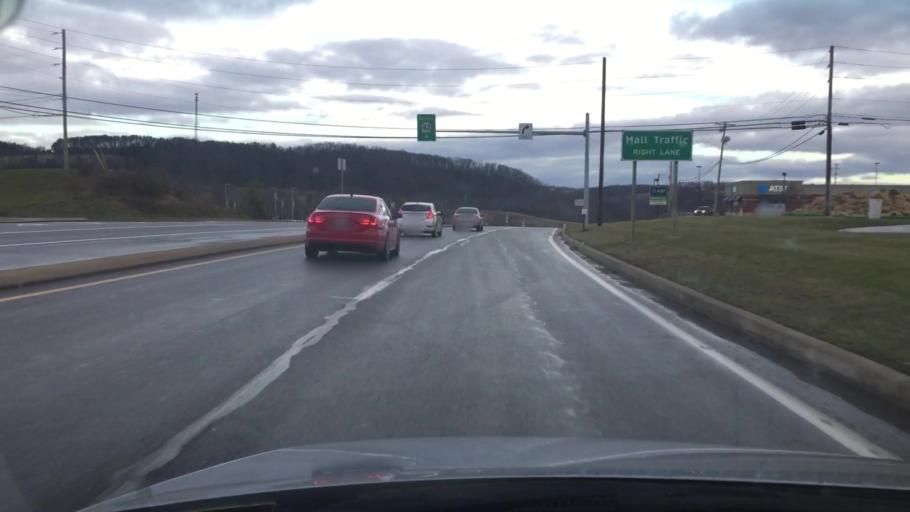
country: US
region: Pennsylvania
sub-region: Columbia County
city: Bloomsburg
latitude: 41.0176
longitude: -76.4906
